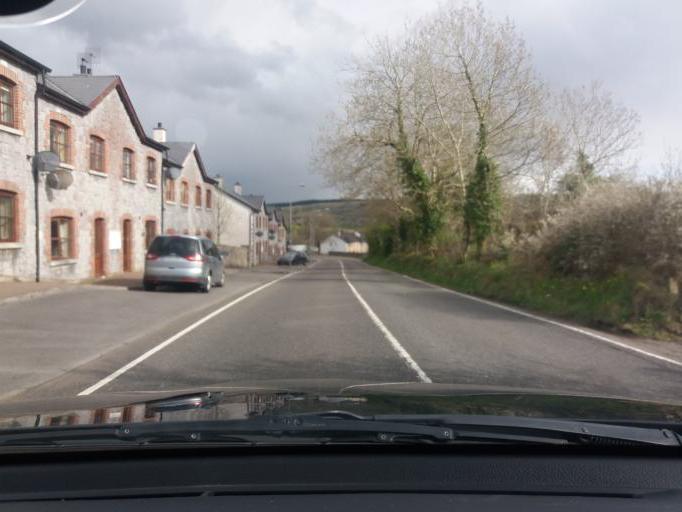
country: IE
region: Connaught
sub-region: County Leitrim
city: Manorhamilton
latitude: 54.3058
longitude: -8.1831
